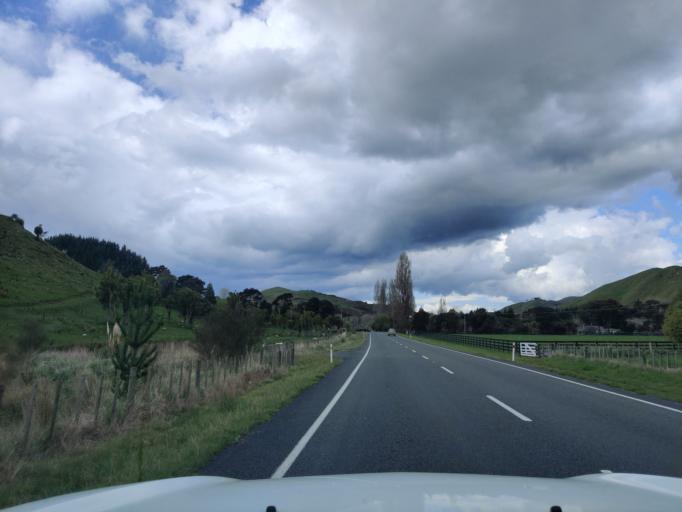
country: NZ
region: Manawatu-Wanganui
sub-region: Wanganui District
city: Wanganui
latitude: -39.8450
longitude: 175.1467
